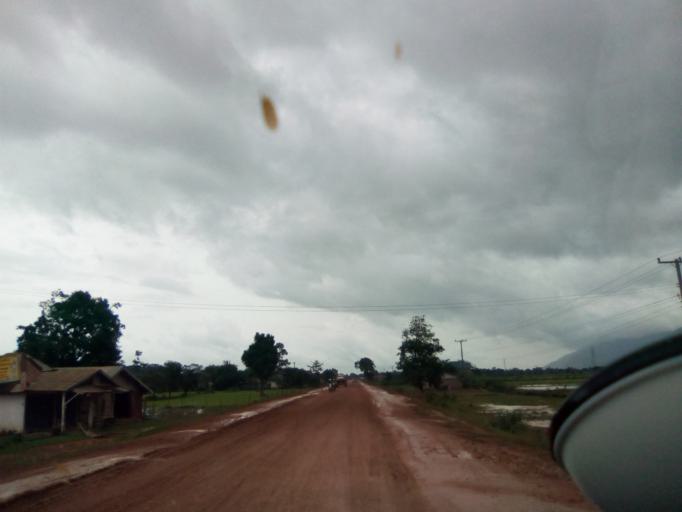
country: LA
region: Attapu
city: Attapu
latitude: 14.7582
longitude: 106.7092
